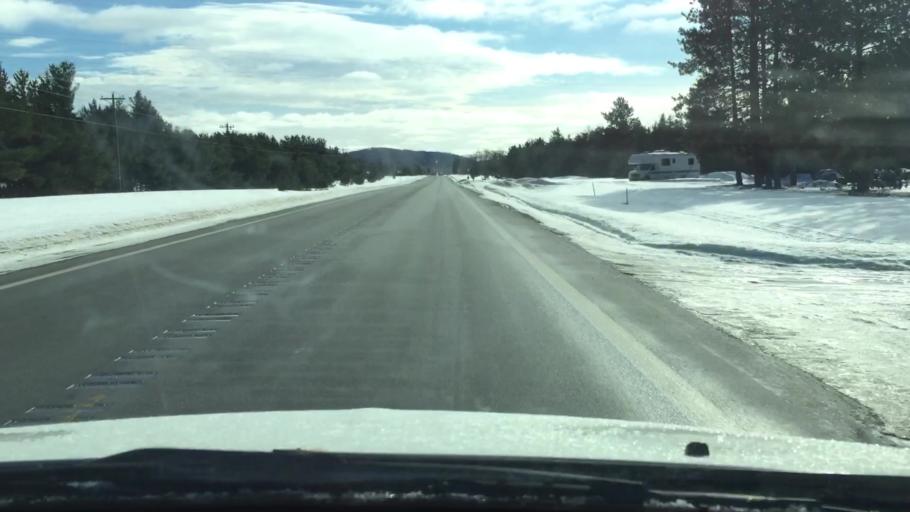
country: US
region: Michigan
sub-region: Antrim County
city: Mancelona
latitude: 44.9216
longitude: -85.0510
